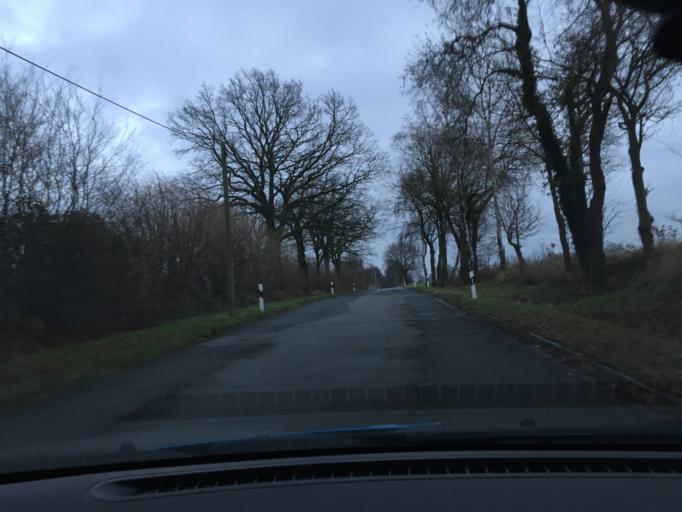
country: DE
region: Mecklenburg-Vorpommern
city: Nostorf
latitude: 53.3985
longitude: 10.6830
